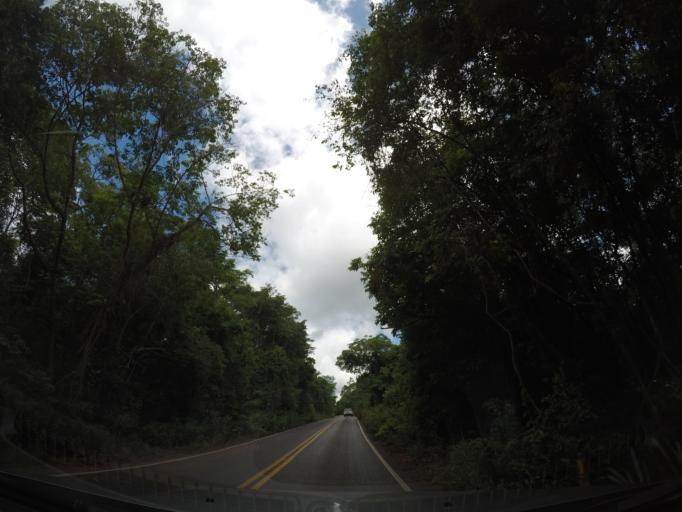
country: BR
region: Bahia
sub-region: Andarai
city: Vera Cruz
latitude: -12.5063
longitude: -41.3620
